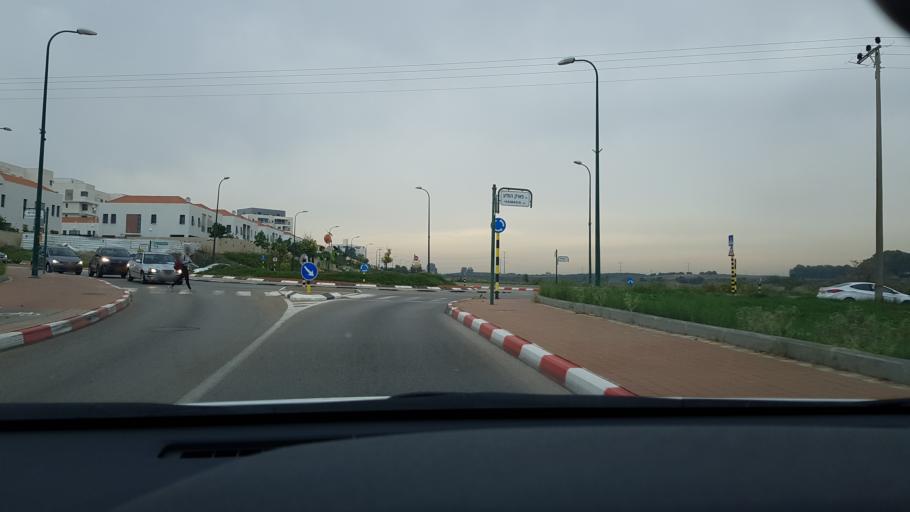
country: IL
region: Central District
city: Ness Ziona
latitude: 31.9211
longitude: 34.8042
